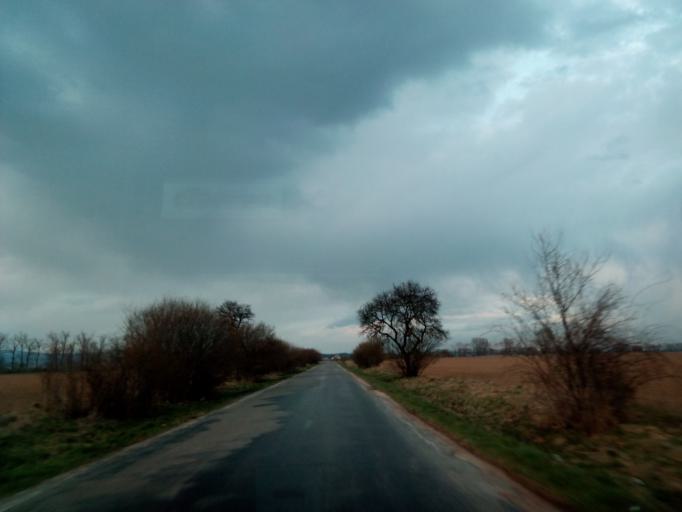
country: SK
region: Kosicky
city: Moldava nad Bodvou
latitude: 48.5750
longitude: 20.9737
